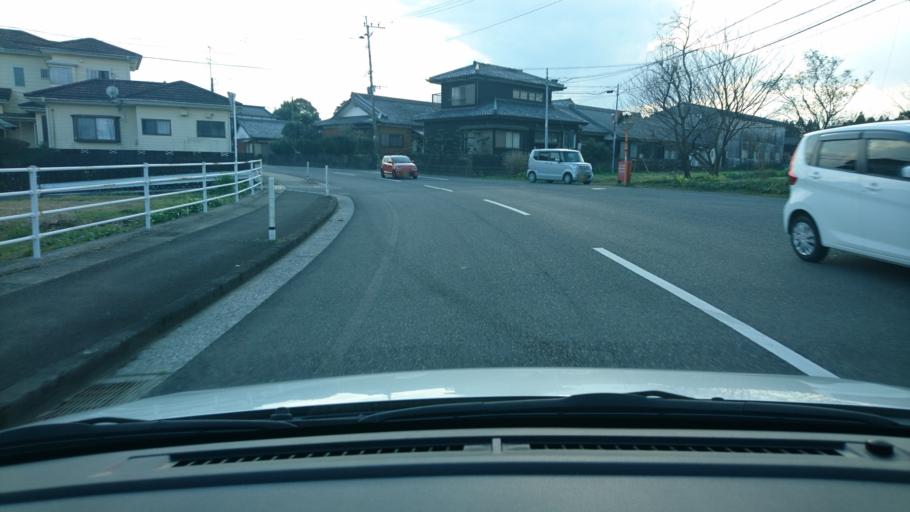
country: JP
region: Miyazaki
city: Miyazaki-shi
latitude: 31.8633
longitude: 131.4002
